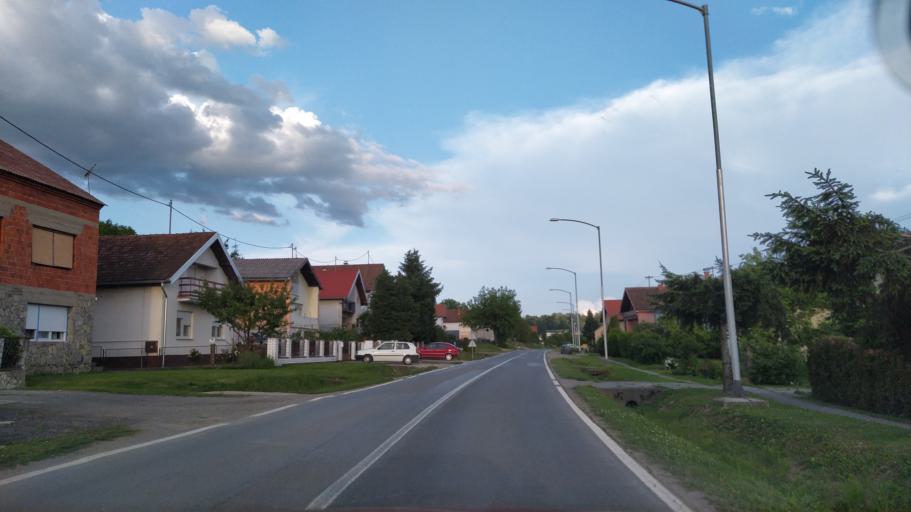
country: HR
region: Osjecko-Baranjska
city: Martin
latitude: 45.4913
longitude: 18.0677
